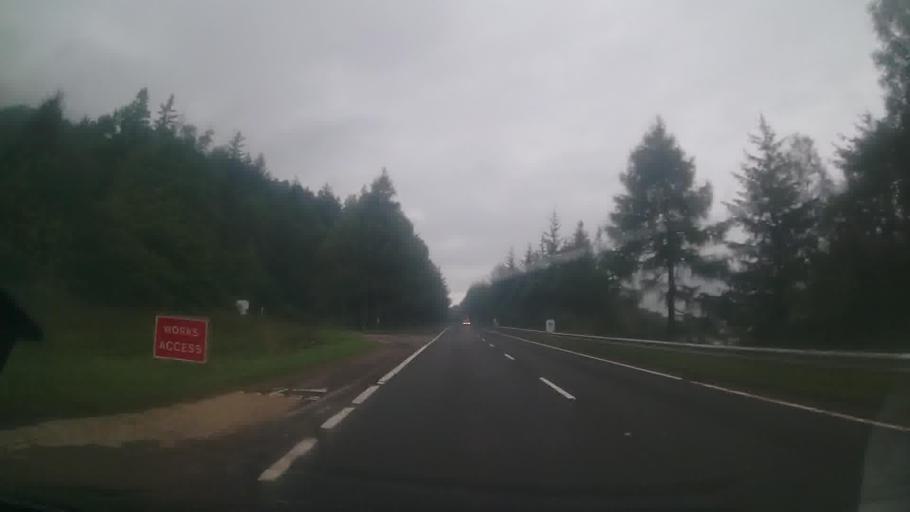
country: GB
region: Scotland
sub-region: Highland
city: Fort William
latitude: 56.6793
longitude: -5.1567
